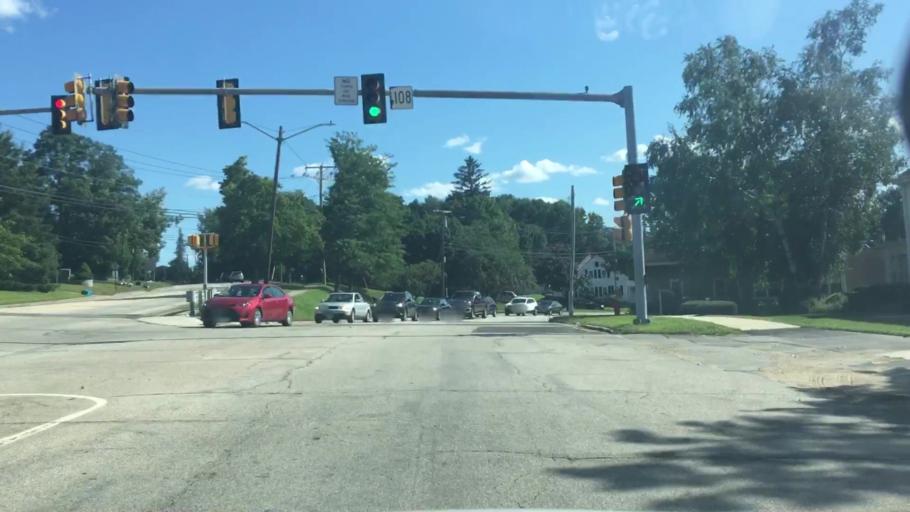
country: US
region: New Hampshire
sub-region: Strafford County
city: Dover
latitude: 43.1848
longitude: -70.8736
